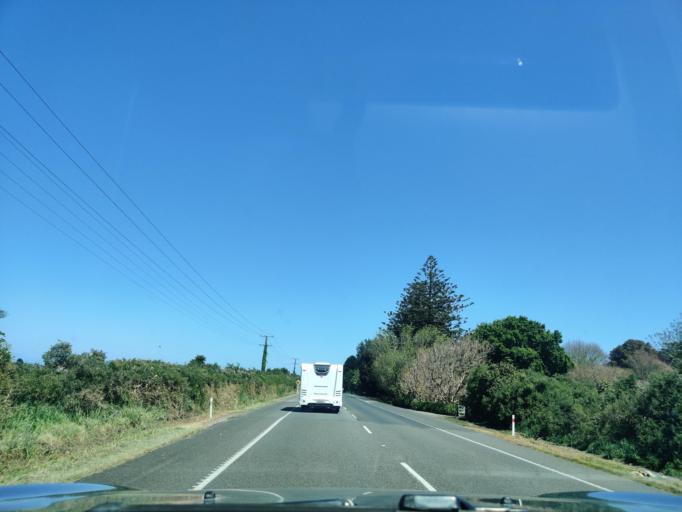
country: NZ
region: Taranaki
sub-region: South Taranaki District
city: Patea
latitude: -39.8082
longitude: 174.7545
